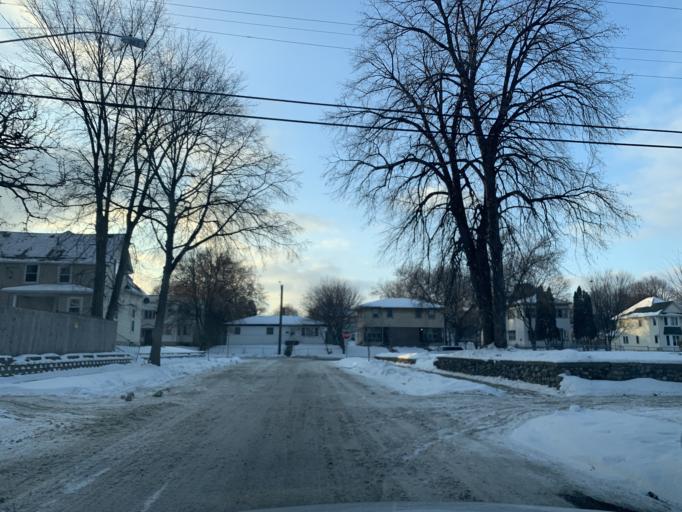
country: US
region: Minnesota
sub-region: Hennepin County
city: Minneapolis
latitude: 44.9890
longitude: -93.3012
